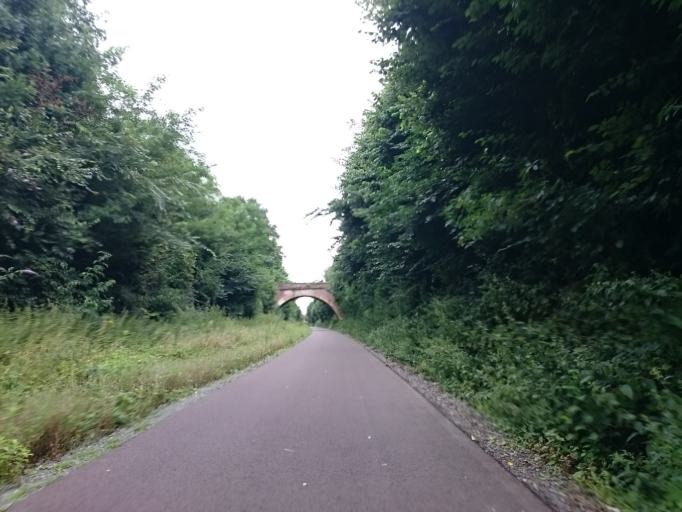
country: FR
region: Lower Normandy
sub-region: Departement du Calvados
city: Saint-Andre-sur-Orne
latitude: 49.1212
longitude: -0.3976
